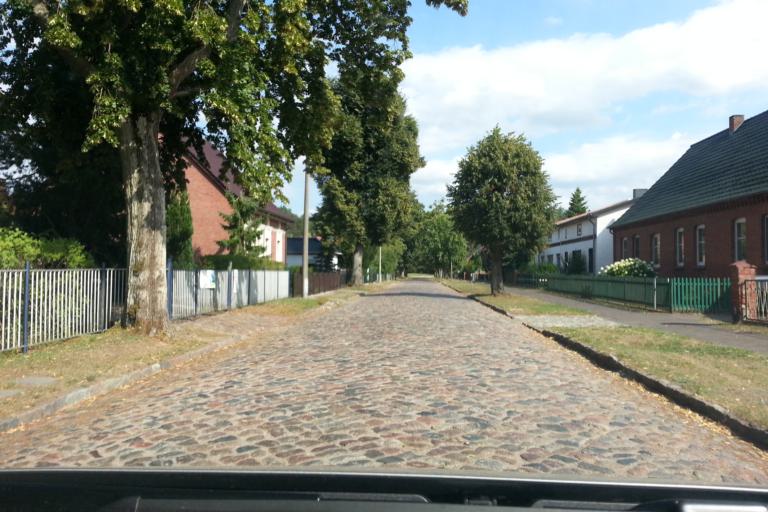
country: DE
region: Mecklenburg-Vorpommern
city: Ferdinandshof
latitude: 53.6295
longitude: 13.8627
